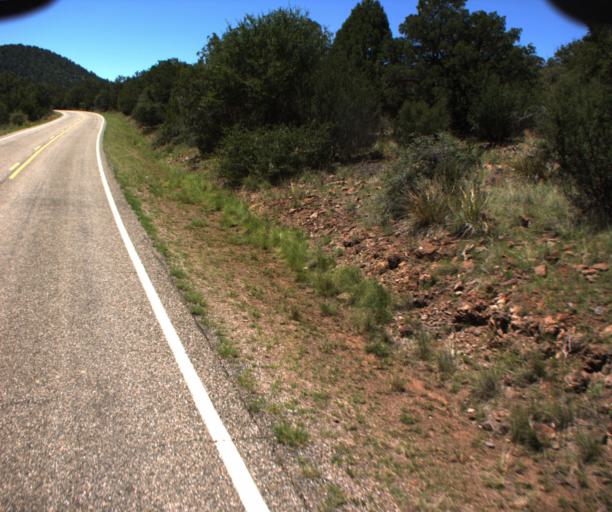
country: US
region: Arizona
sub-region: Greenlee County
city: Morenci
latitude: 33.2470
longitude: -109.3718
